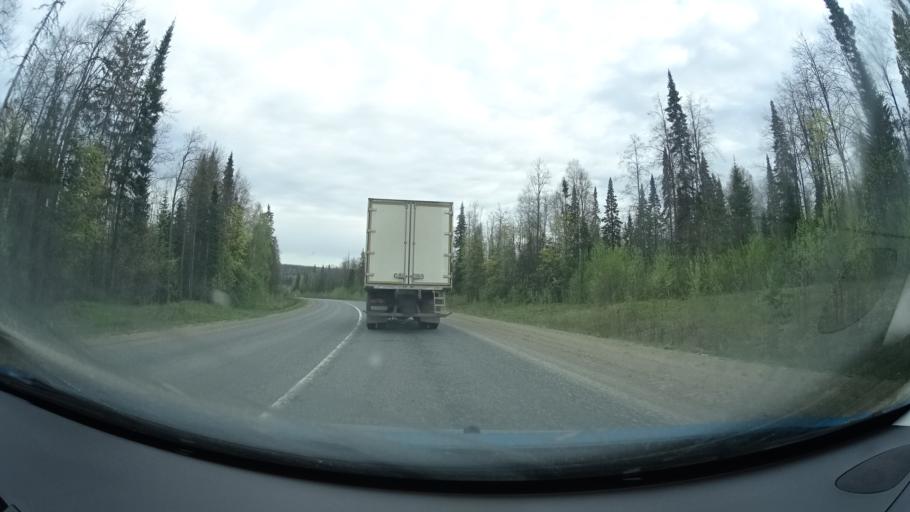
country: RU
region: Perm
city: Yugo-Kamskiy
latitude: 57.5981
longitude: 55.6538
